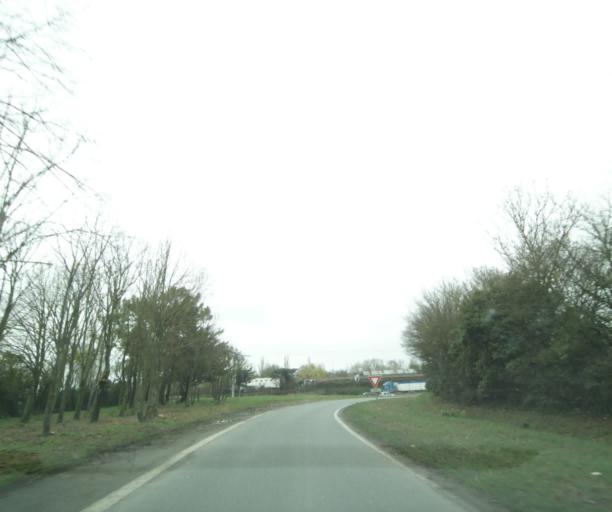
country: FR
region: Poitou-Charentes
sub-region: Departement de la Charente-Maritime
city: La Rochelle
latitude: 46.1737
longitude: -1.1744
